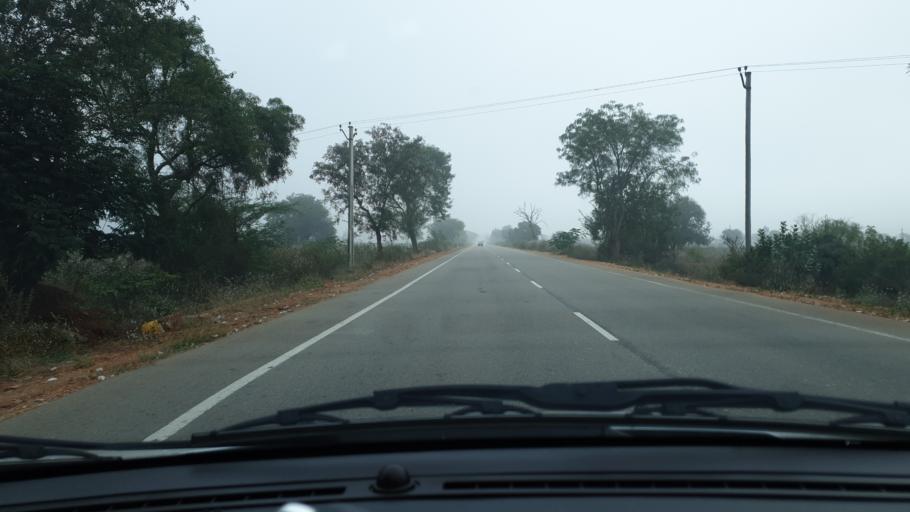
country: IN
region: Telangana
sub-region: Nalgonda
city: Devarkonda
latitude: 16.6356
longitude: 78.6206
